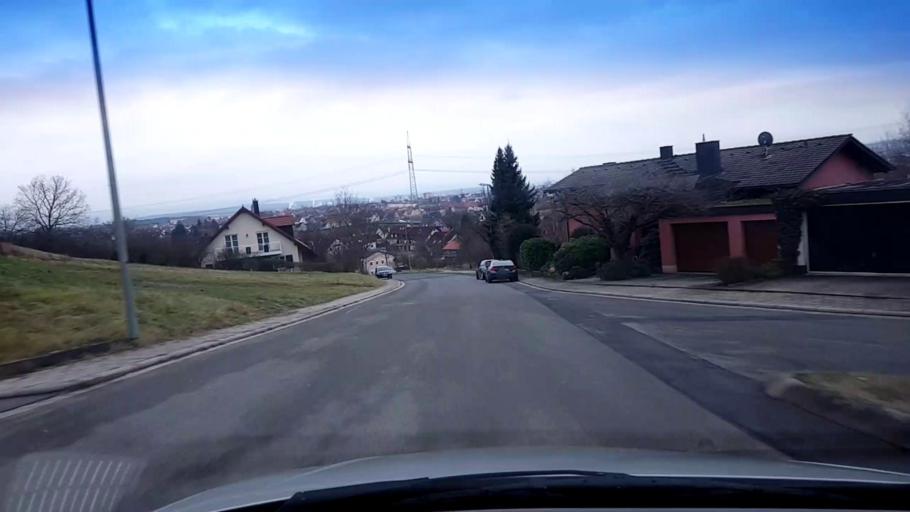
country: DE
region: Bavaria
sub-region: Upper Franconia
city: Hallstadt
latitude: 49.9335
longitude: 10.8604
